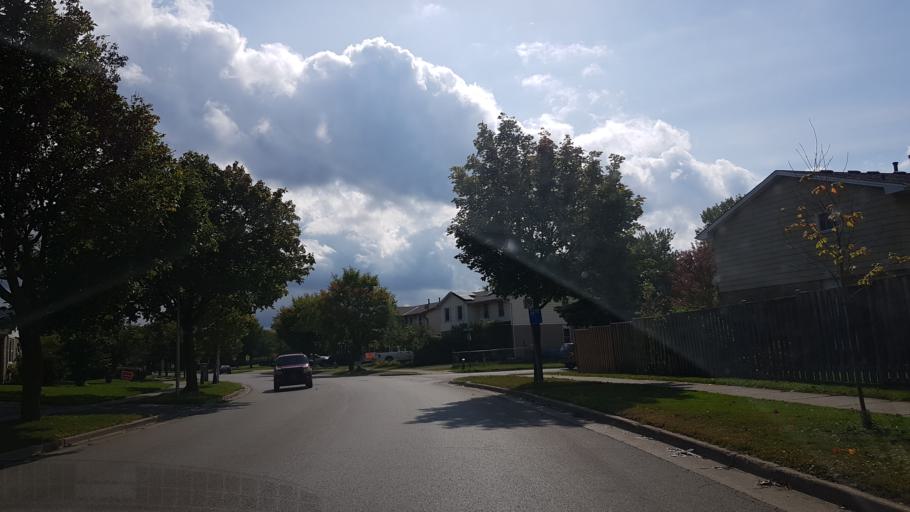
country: CA
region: Ontario
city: London
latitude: 42.9392
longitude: -81.2388
